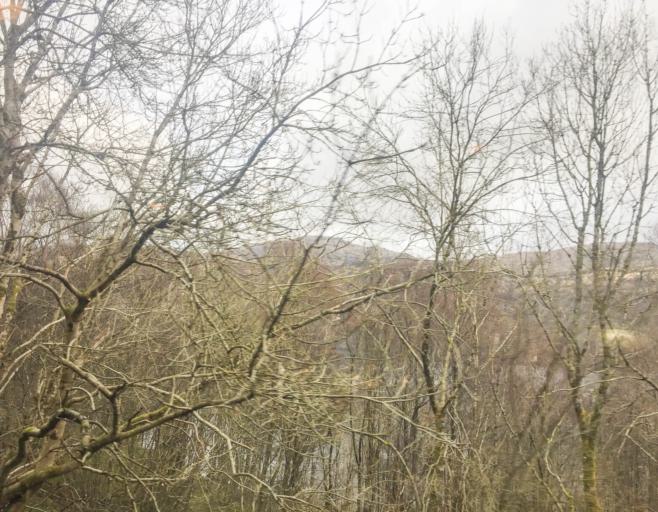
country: GB
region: Scotland
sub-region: Argyll and Bute
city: Garelochhead
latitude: 56.2553
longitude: -4.7100
